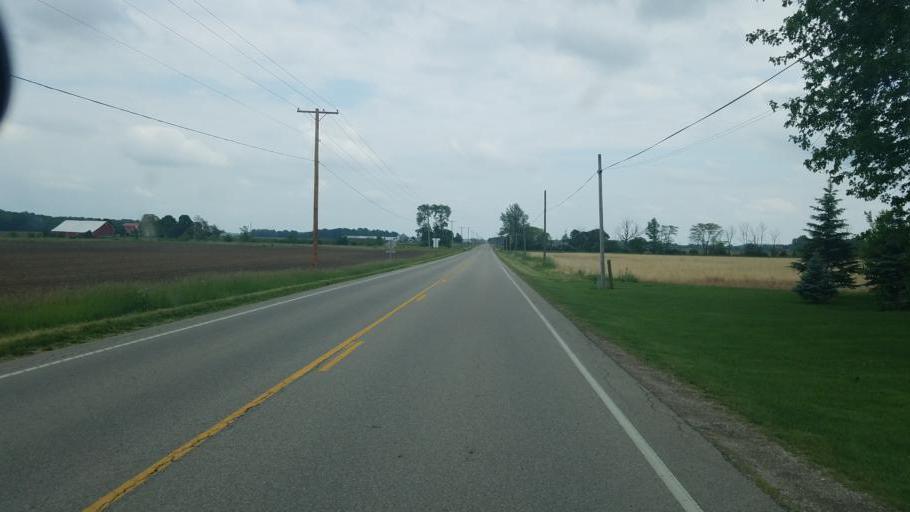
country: US
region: Ohio
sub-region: Union County
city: New California
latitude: 40.1951
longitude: -83.2960
